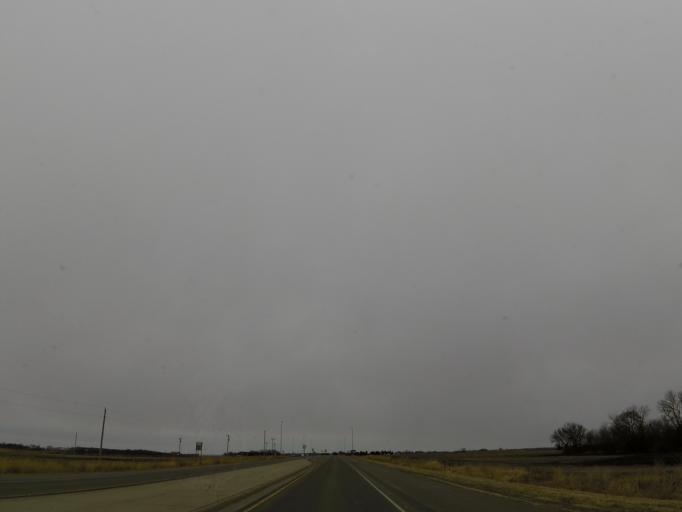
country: US
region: Minnesota
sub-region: Le Sueur County
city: Le Sueur
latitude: 44.5431
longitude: -93.8571
